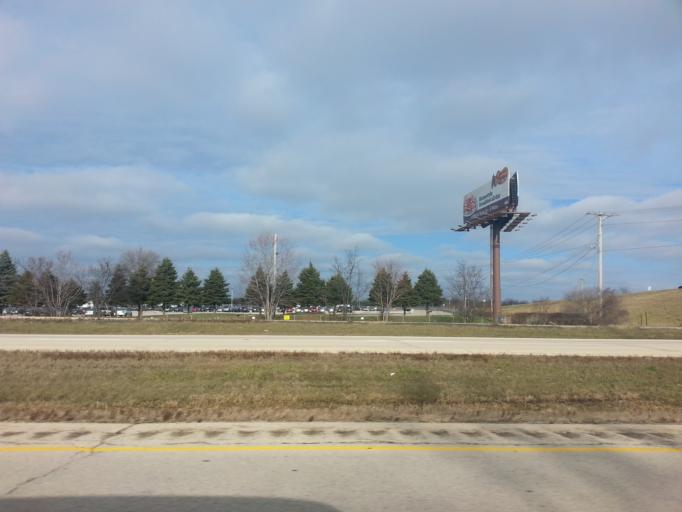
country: US
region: Illinois
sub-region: Winnebago County
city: Cherry Valley
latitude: 42.2201
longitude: -88.9999
